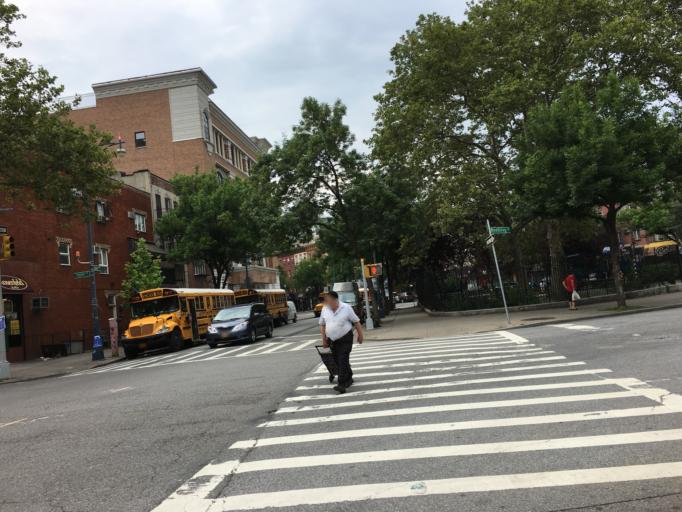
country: US
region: New York
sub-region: Queens County
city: Long Island City
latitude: 40.7070
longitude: -73.9612
